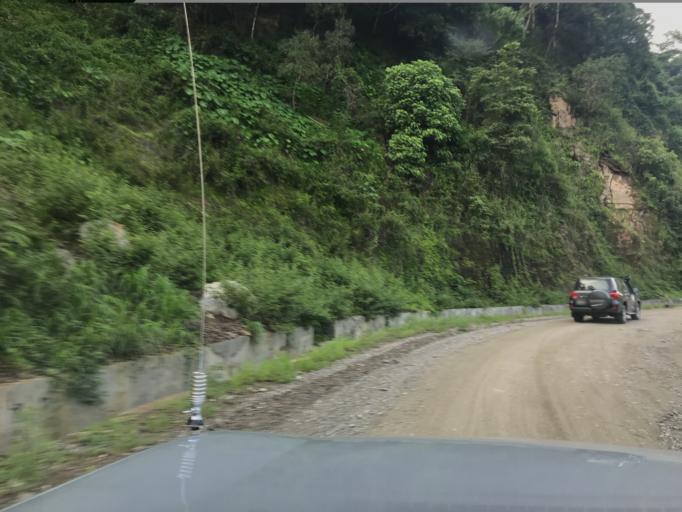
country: TL
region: Dili
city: Dili
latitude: -8.6358
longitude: 125.5141
